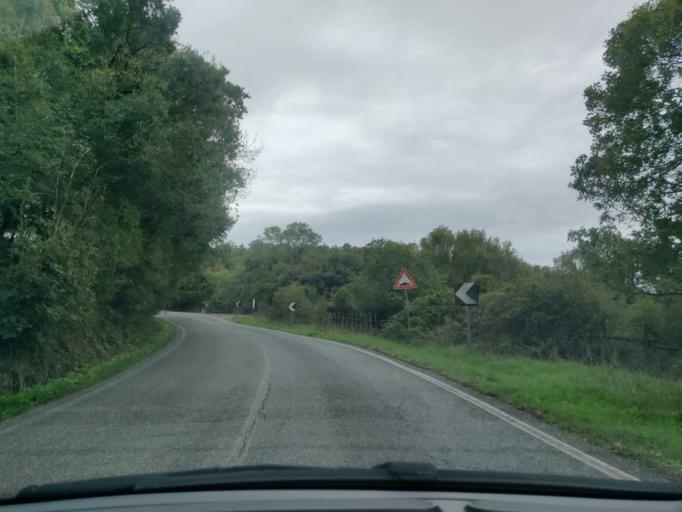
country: IT
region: Latium
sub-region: Citta metropolitana di Roma Capitale
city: Allumiere
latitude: 42.1388
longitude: 11.8720
